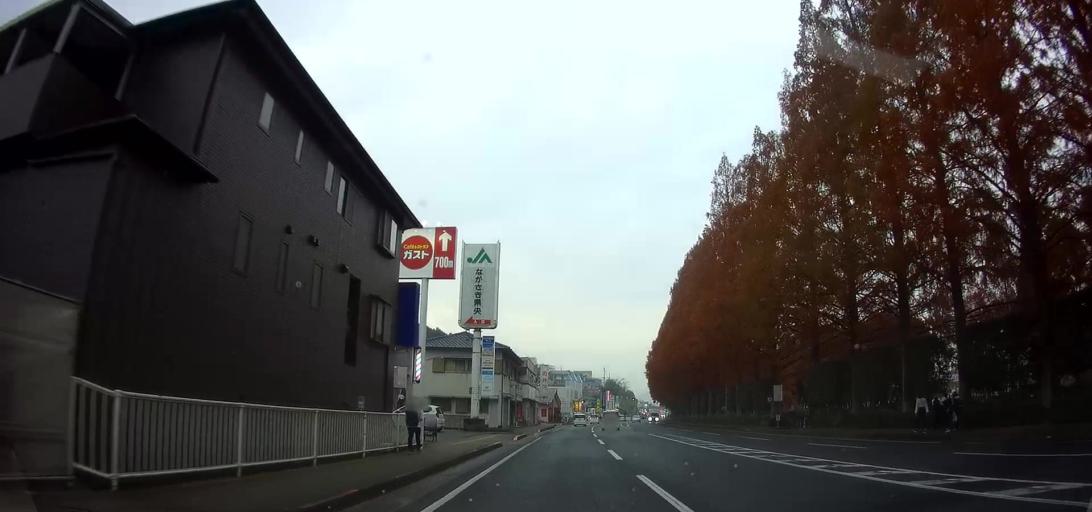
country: JP
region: Nagasaki
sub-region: Isahaya-shi
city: Isahaya
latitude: 32.8345
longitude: 130.0416
